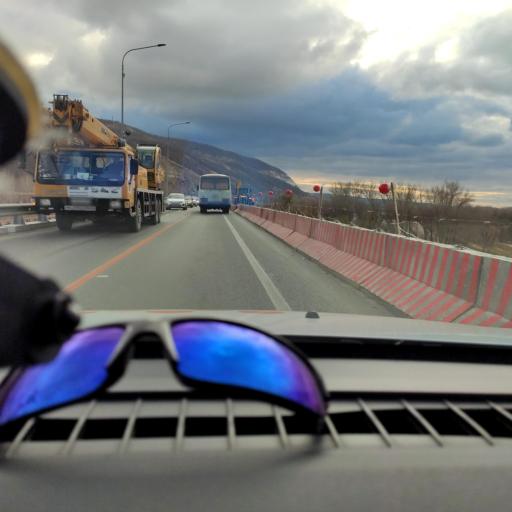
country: RU
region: Samara
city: Volzhskiy
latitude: 53.4119
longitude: 50.1371
